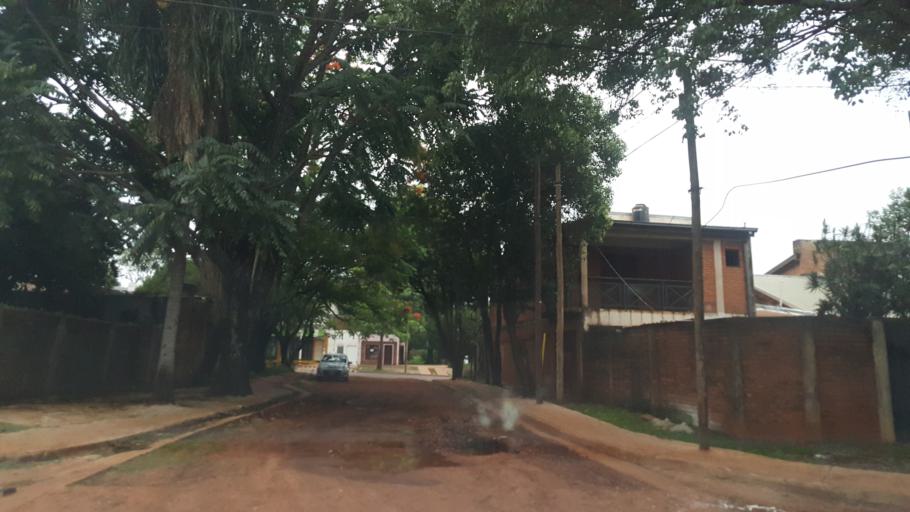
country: AR
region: Misiones
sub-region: Departamento de Capital
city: Posadas
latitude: -27.3705
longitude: -55.9273
